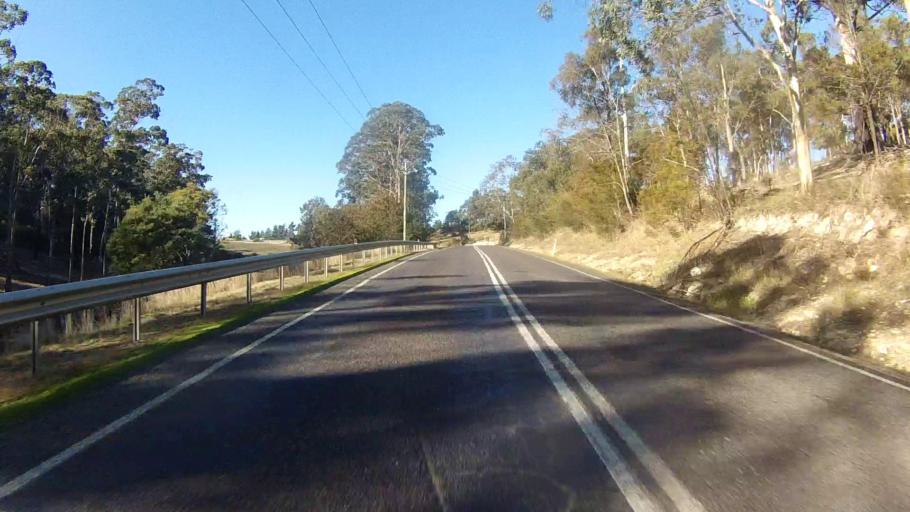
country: AU
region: Tasmania
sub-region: Sorell
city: Sorell
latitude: -42.8155
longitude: 147.6646
